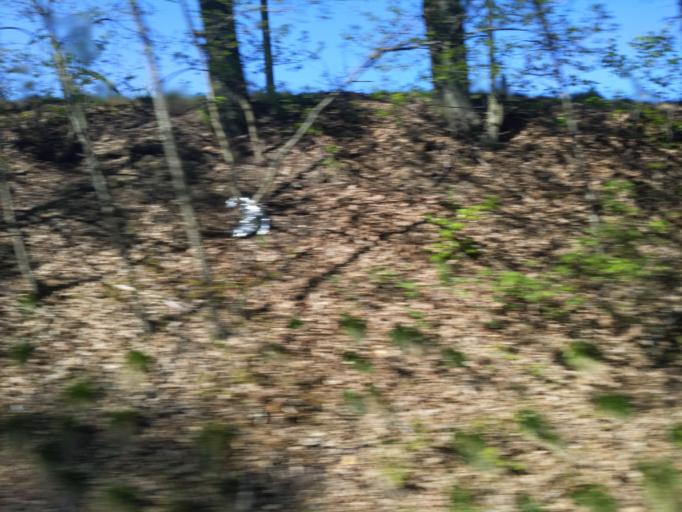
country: DE
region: Saxony
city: Demitz-Thumitz
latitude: 51.1427
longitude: 14.2381
